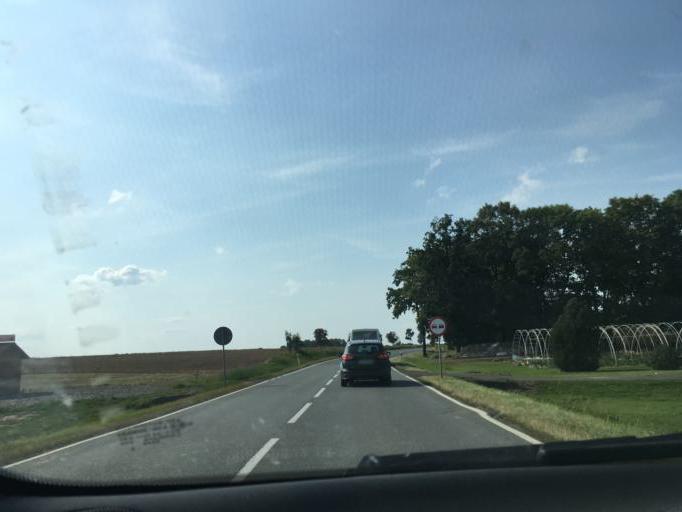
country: PL
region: Opole Voivodeship
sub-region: Powiat prudnicki
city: Prudnik
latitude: 50.3652
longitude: 17.5423
